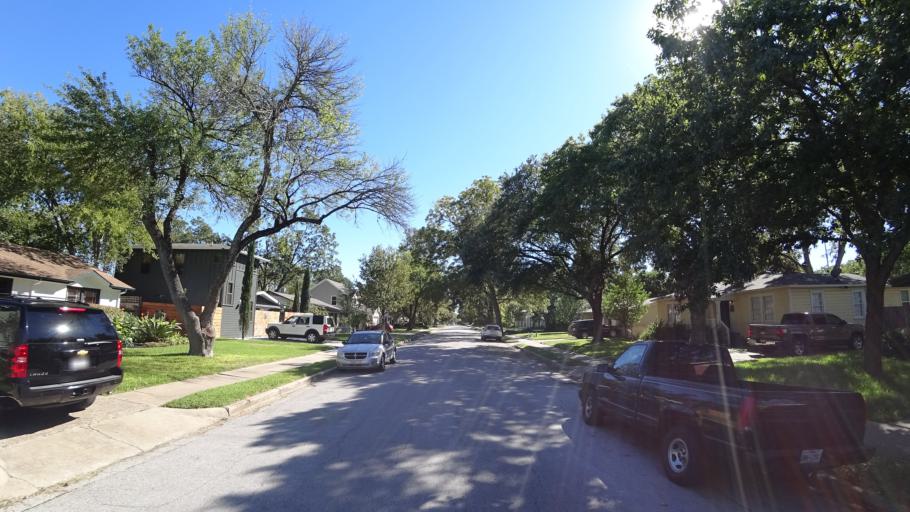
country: US
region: Texas
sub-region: Travis County
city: West Lake Hills
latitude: 30.3291
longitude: -97.7540
